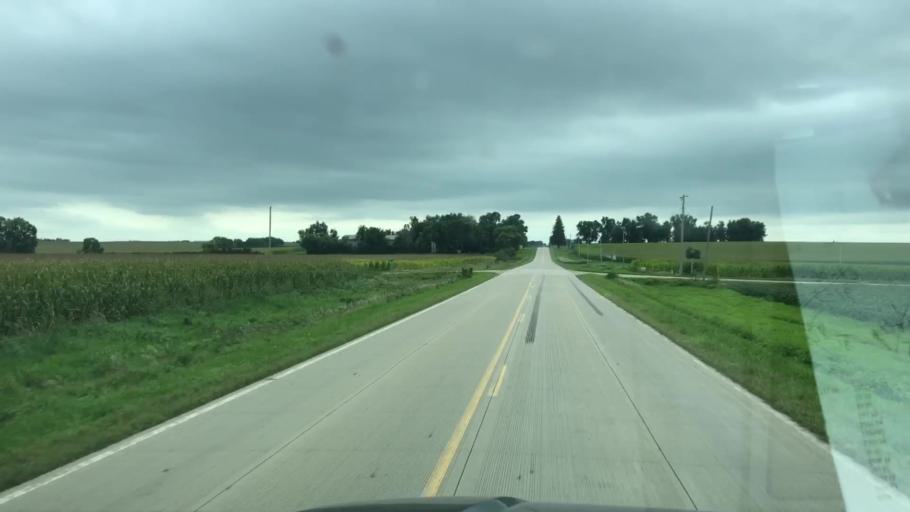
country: US
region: Iowa
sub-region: Sioux County
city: Alton
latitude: 43.1140
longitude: -95.9788
